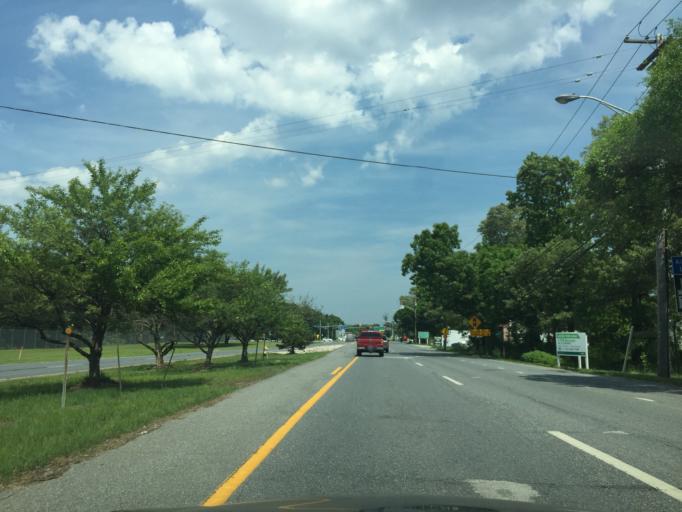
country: US
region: Maryland
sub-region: Anne Arundel County
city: Ferndale
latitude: 39.1643
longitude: -76.6494
